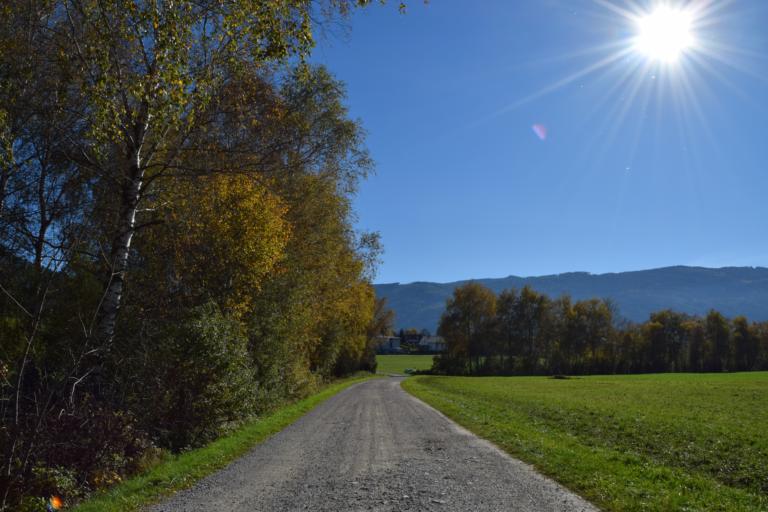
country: AT
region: Styria
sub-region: Politischer Bezirk Liezen
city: Irdning
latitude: 47.5104
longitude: 14.1046
